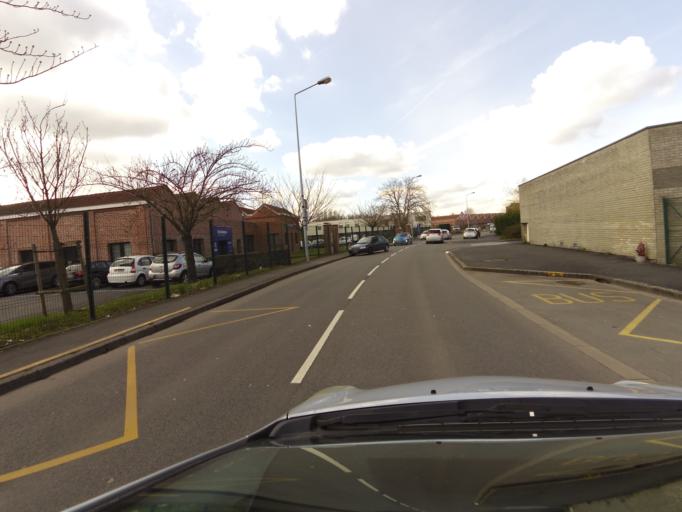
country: FR
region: Nord-Pas-de-Calais
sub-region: Departement du Nord
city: Armentieres
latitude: 50.6875
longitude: 2.8662
